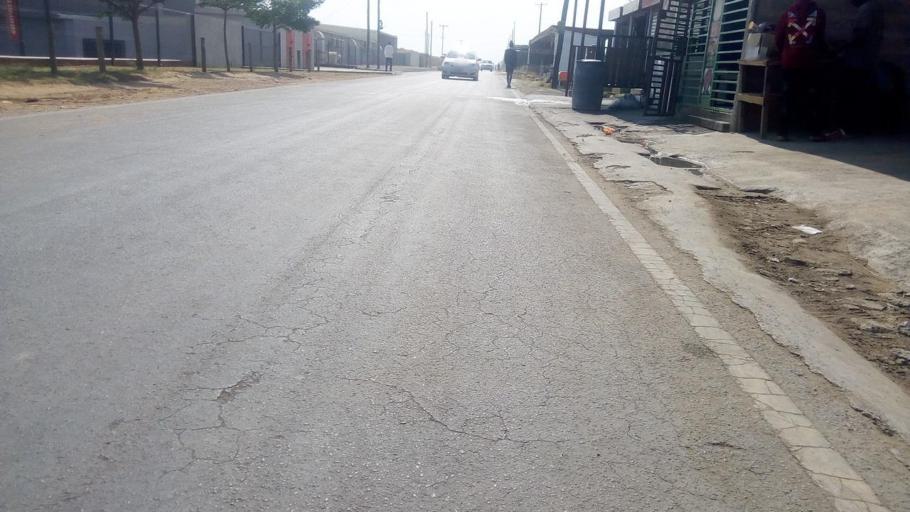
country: ZM
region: Lusaka
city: Lusaka
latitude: -15.3627
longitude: 28.2774
